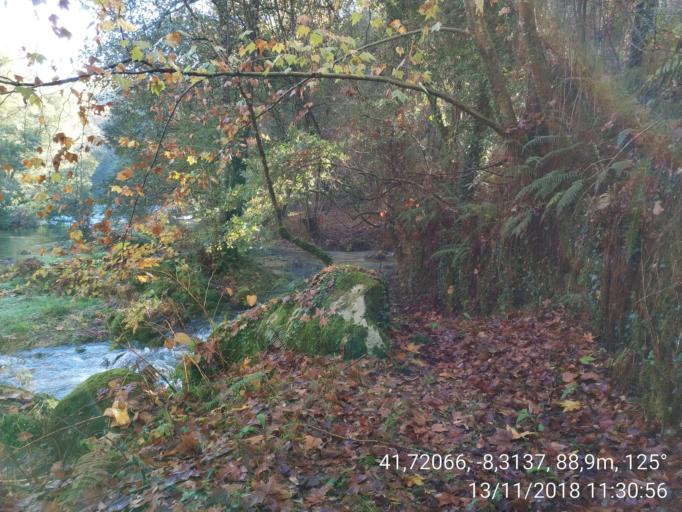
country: PT
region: Braga
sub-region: Terras de Bouro
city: Terras de Bouro
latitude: 41.7207
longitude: -8.3137
